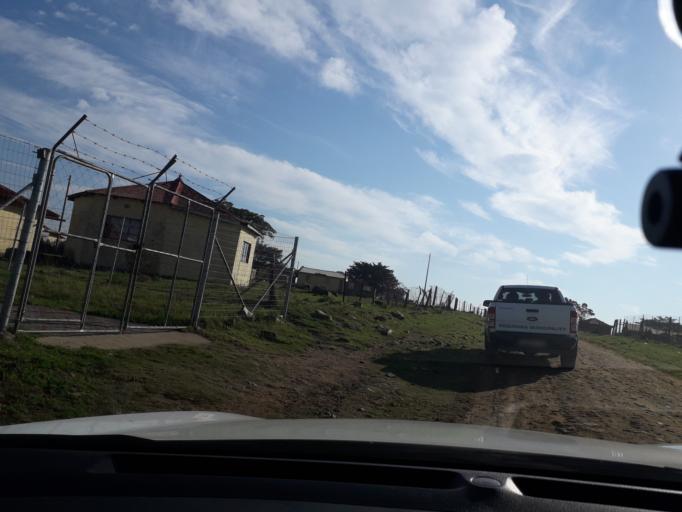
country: ZA
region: Eastern Cape
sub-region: Buffalo City Metropolitan Municipality
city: Bhisho
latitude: -32.9379
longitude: 27.2903
